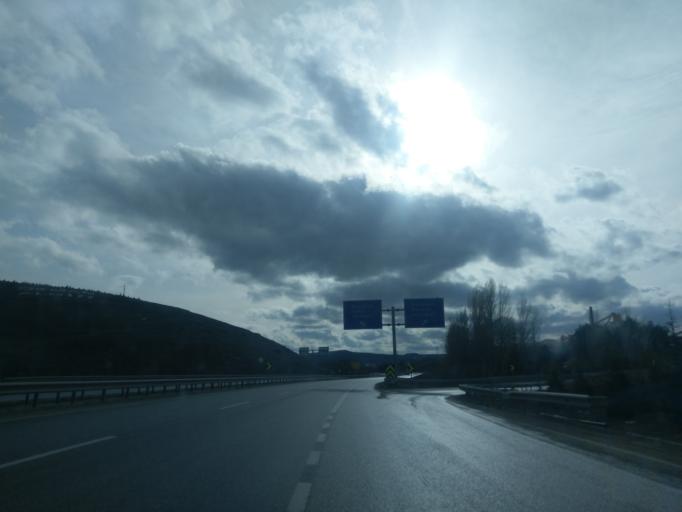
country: TR
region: Eskisehir
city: Inonu
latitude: 39.7086
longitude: 30.1572
